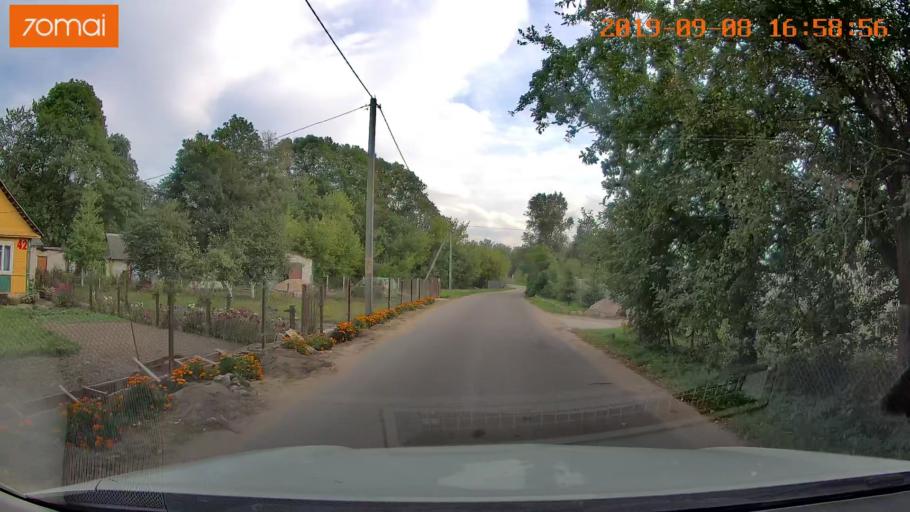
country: BY
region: Grodnenskaya
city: Hrodna
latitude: 53.7244
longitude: 23.9323
